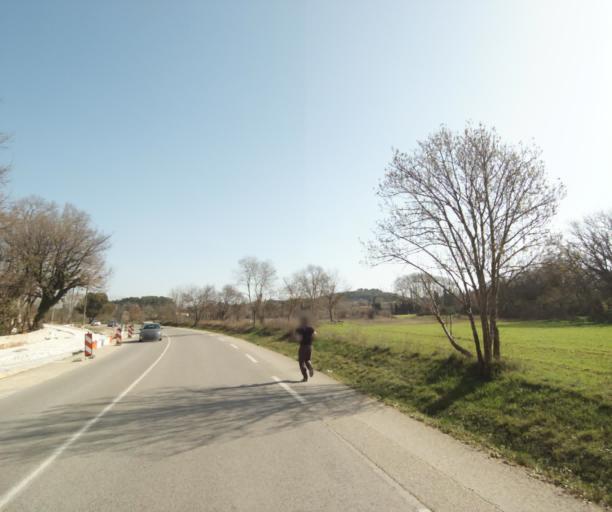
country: FR
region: Provence-Alpes-Cote d'Azur
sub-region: Departement des Bouches-du-Rhone
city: Aix-en-Provence
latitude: 43.5078
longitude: 5.4274
